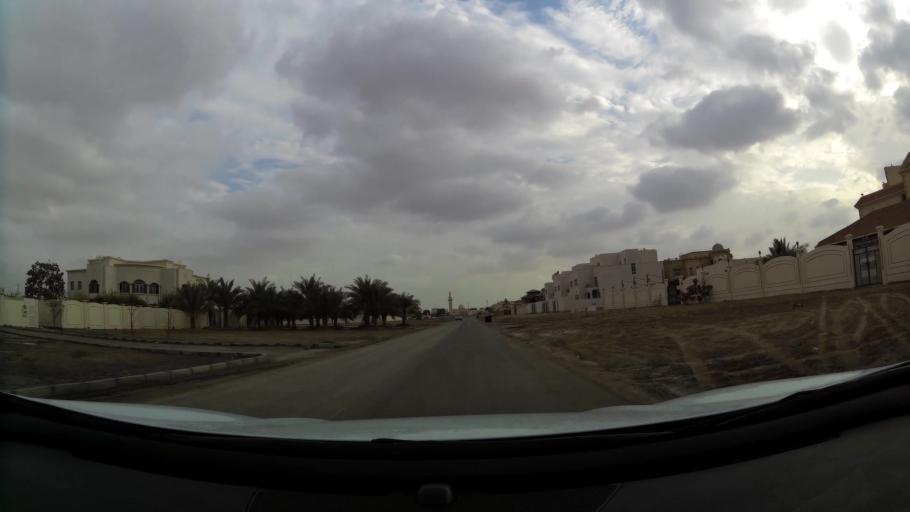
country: AE
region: Abu Dhabi
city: Abu Dhabi
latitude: 24.3590
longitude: 54.5454
